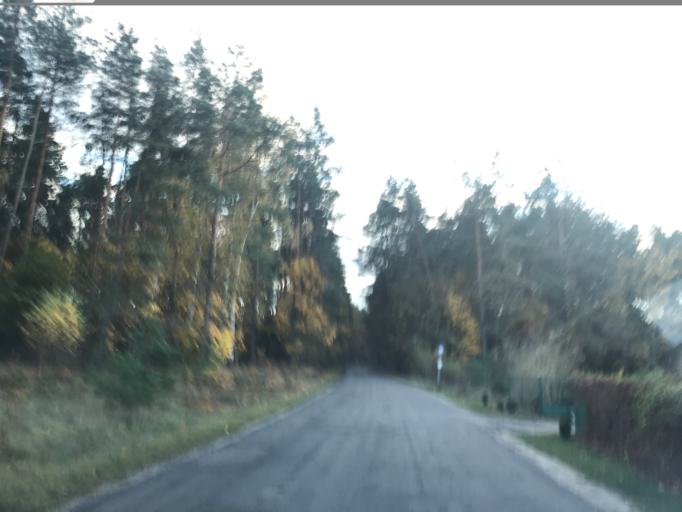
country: PL
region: Warmian-Masurian Voivodeship
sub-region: Powiat dzialdowski
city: Lidzbark
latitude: 53.2337
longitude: 19.7965
